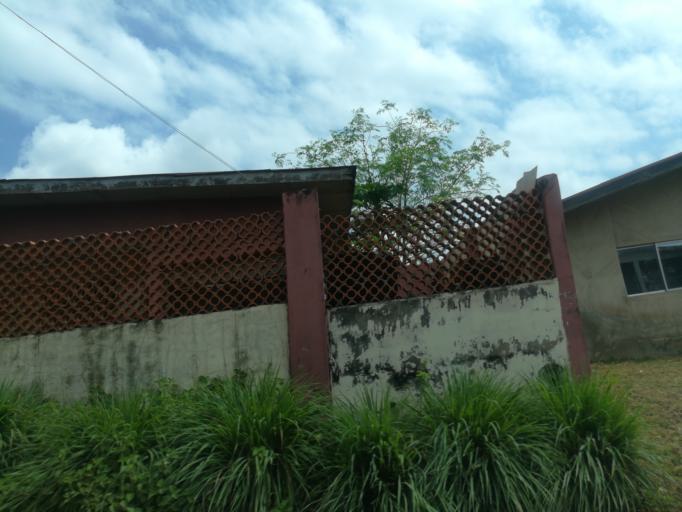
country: NG
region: Oyo
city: Egbeda
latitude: 7.4220
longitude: 3.9979
